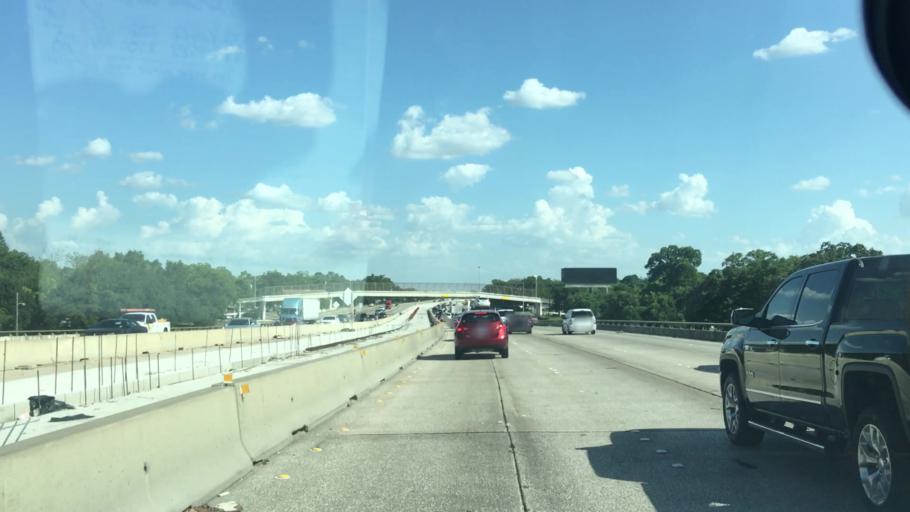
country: US
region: Texas
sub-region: Dallas County
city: Dallas
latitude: 32.7603
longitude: -96.7744
